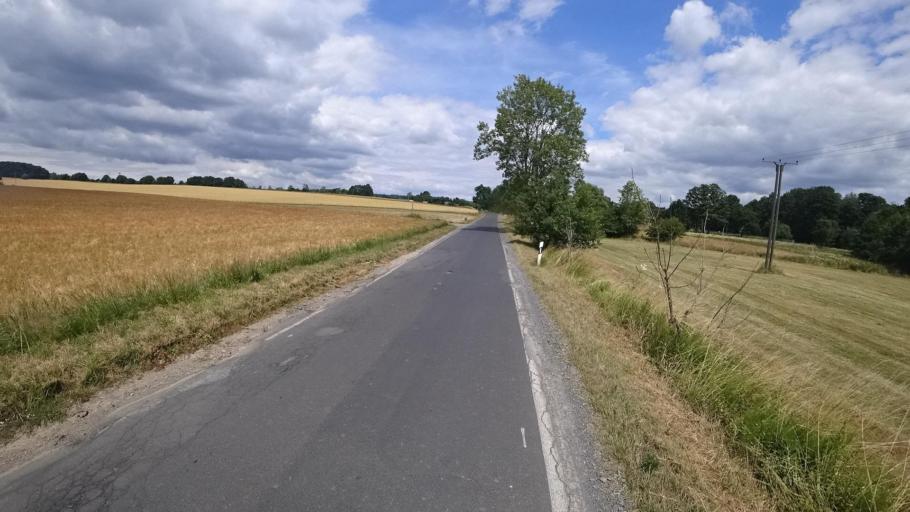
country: DE
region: Rheinland-Pfalz
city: Forstmehren
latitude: 50.7046
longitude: 7.5317
